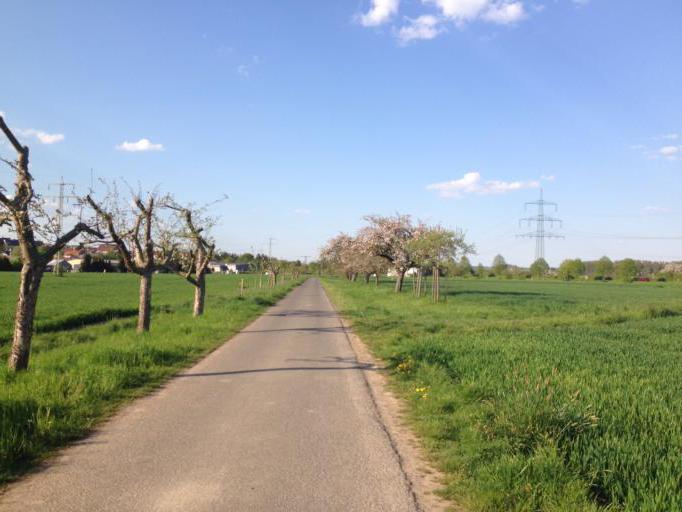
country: DE
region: Hesse
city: Lollar
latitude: 50.6272
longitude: 8.6786
